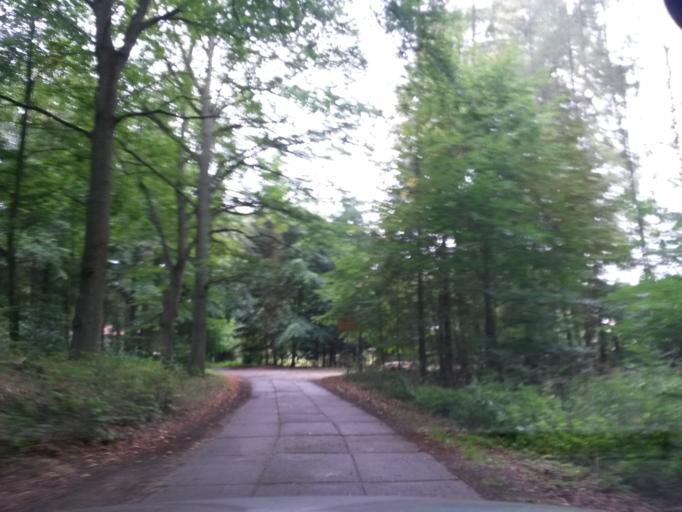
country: DE
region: Brandenburg
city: Althuttendorf
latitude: 53.0781
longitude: 13.8305
